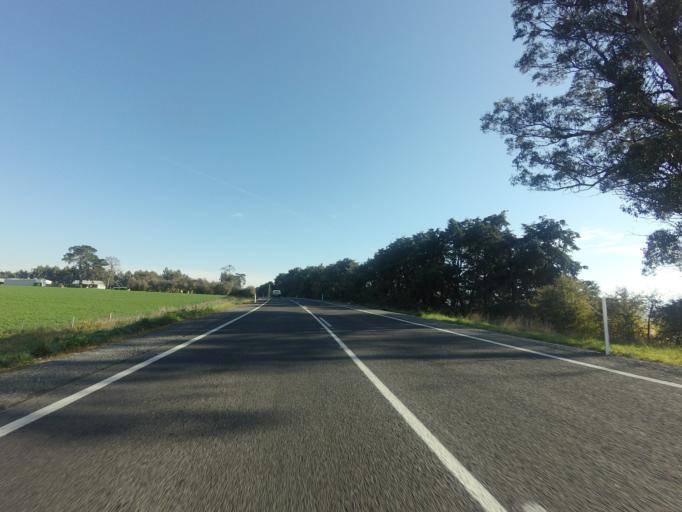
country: AU
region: Tasmania
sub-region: Northern Midlands
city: Longford
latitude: -41.5716
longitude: 147.0972
